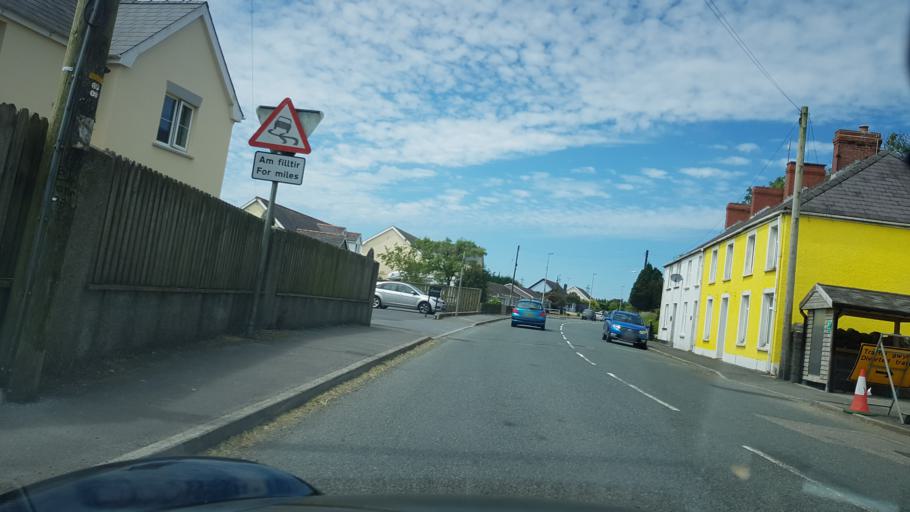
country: GB
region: Wales
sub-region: Carmarthenshire
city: Whitland
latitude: 51.7757
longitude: -4.6049
